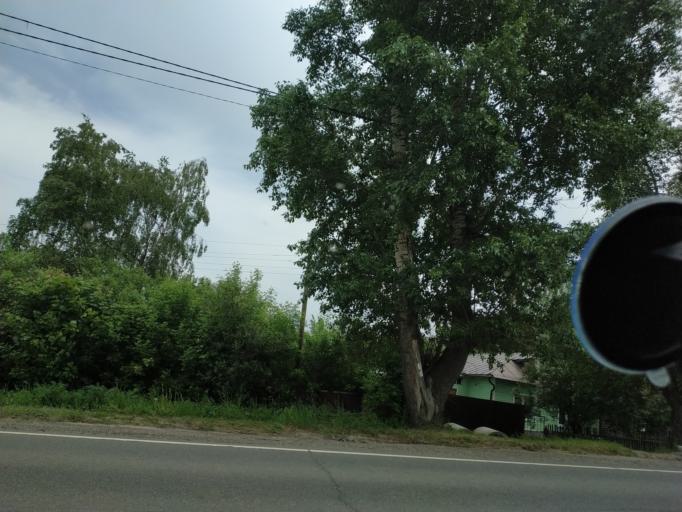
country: RU
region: Moskovskaya
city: Ostrovtsy
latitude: 55.5513
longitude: 38.0619
